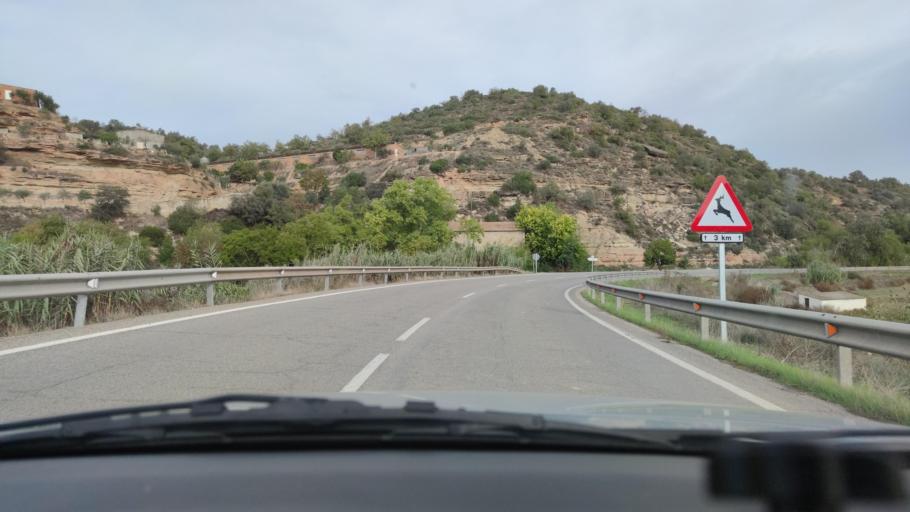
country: ES
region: Catalonia
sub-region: Provincia de Lleida
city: Artesa de Segre
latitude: 41.9110
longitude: 1.0679
